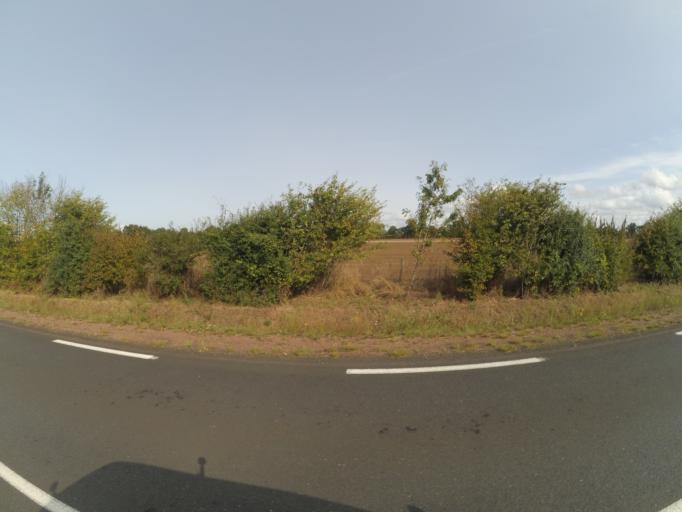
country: FR
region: Pays de la Loire
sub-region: Departement de la Vendee
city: Treize-Septiers
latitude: 46.9806
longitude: -1.2041
